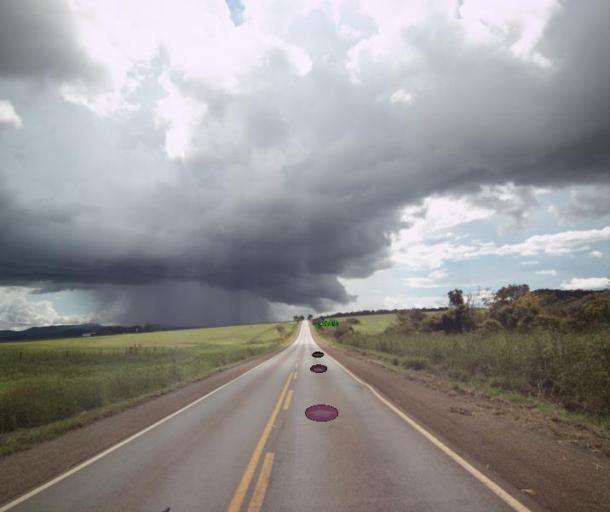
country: BR
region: Goias
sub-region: Uruacu
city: Uruacu
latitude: -14.6684
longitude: -49.1461
